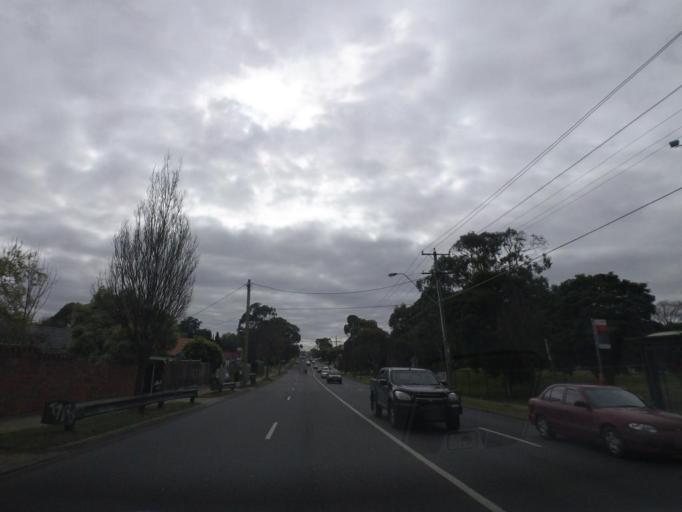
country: AU
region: Victoria
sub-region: Whitehorse
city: Mont Albert North
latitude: -37.8094
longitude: 145.1164
